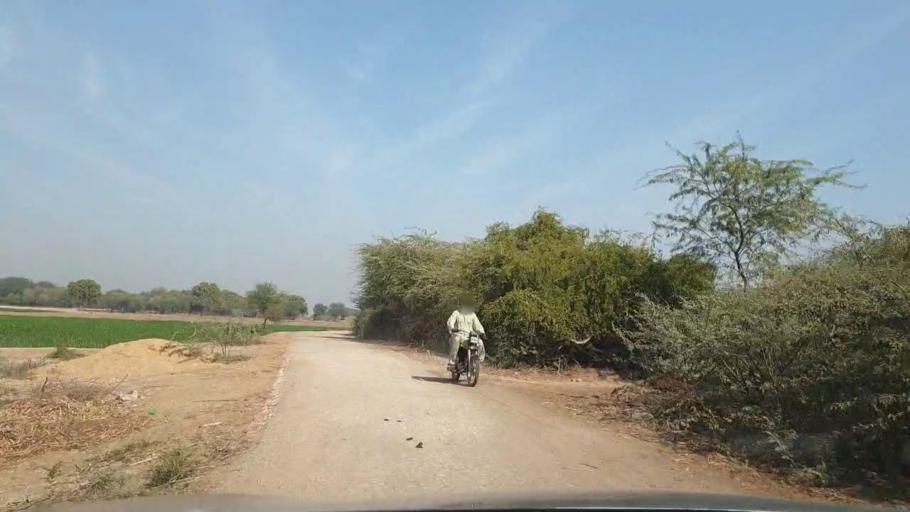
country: PK
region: Sindh
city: Tando Adam
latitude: 25.6394
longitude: 68.7277
